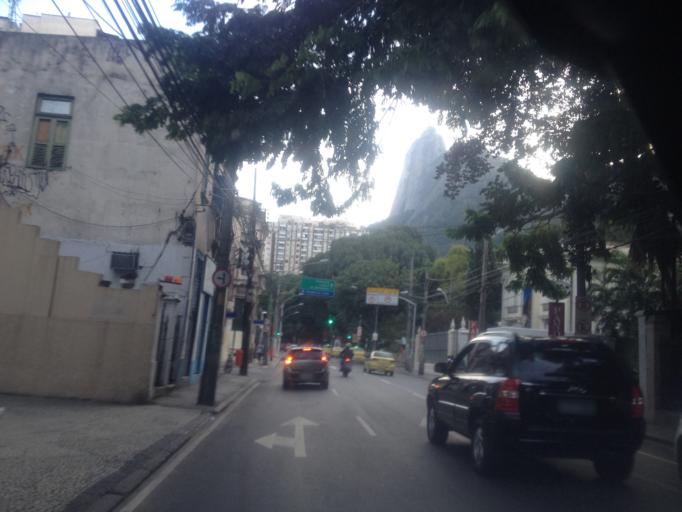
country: BR
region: Rio de Janeiro
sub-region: Rio De Janeiro
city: Rio de Janeiro
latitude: -22.9503
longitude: -43.1916
